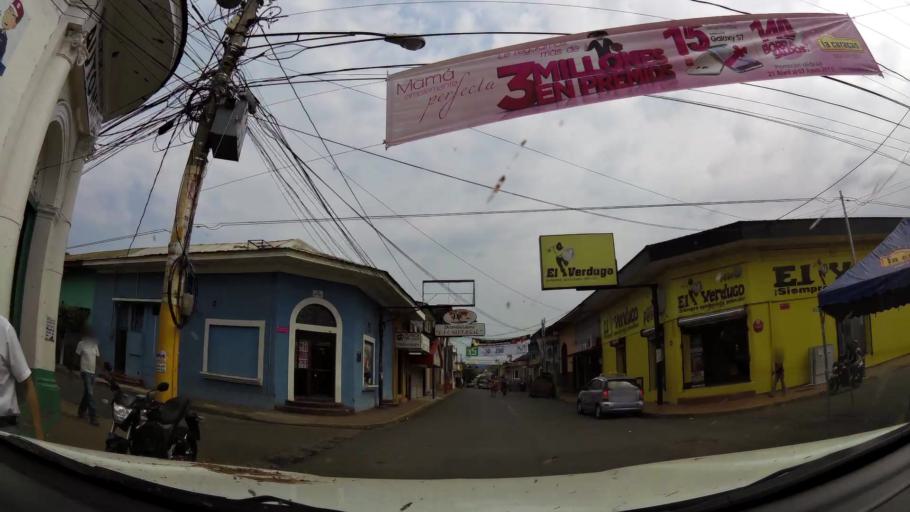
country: NI
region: Masaya
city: Masaya
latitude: 11.9775
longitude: -86.0960
